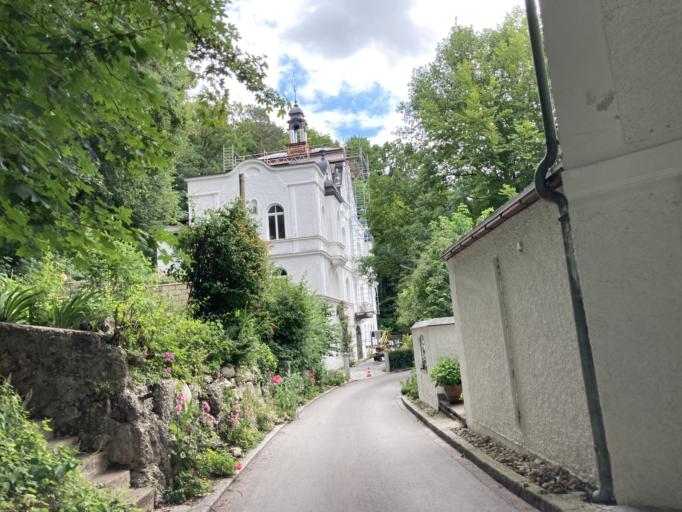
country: DE
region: Bavaria
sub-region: Upper Bavaria
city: Rosenheim
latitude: 47.8783
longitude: 12.1440
